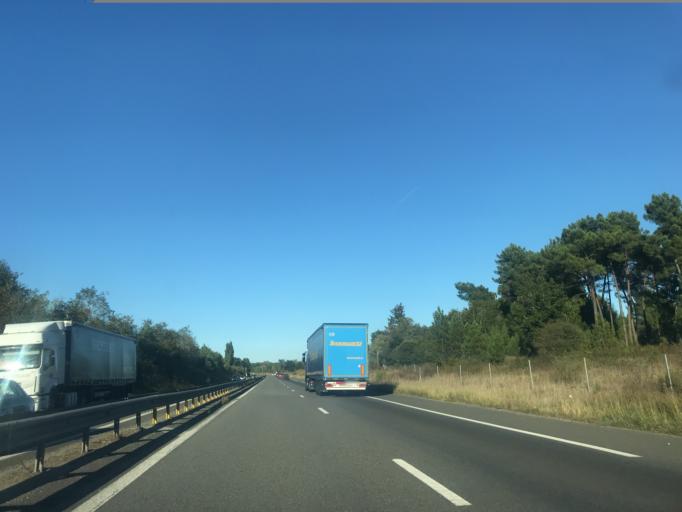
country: FR
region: Aquitaine
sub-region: Departement de la Gironde
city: Laruscade
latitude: 45.1943
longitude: -0.3100
